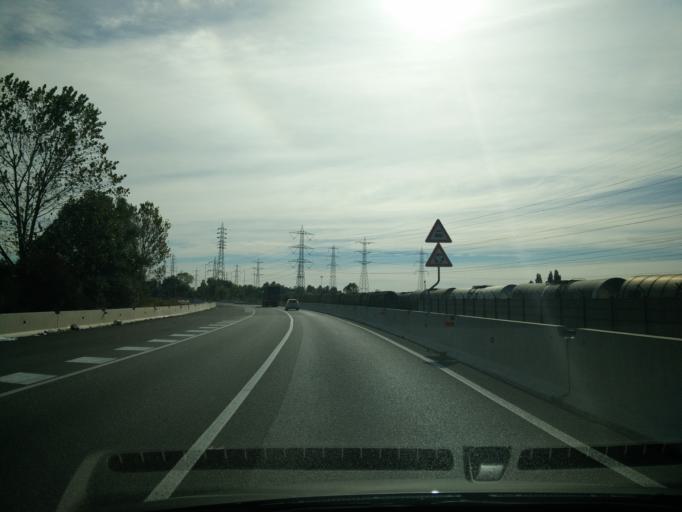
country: IT
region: Veneto
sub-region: Provincia di Venezia
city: Mestre
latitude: 45.4391
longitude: 12.2107
